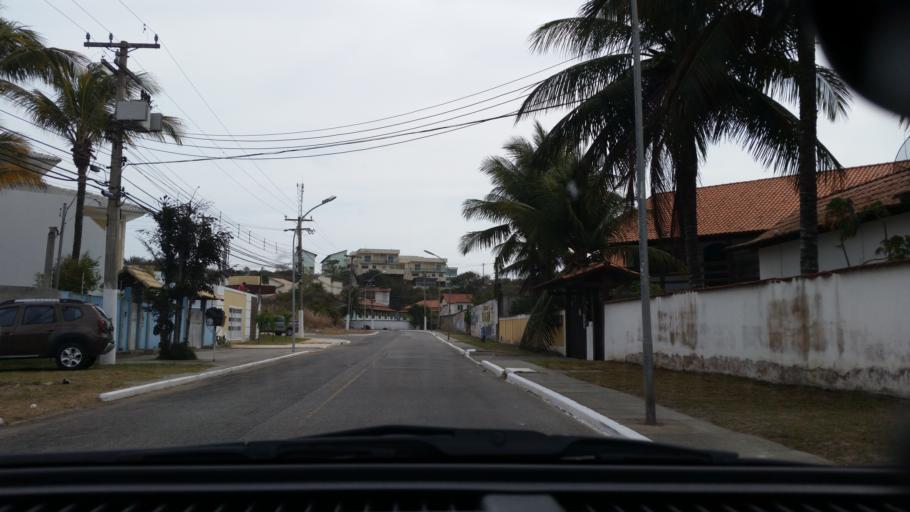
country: BR
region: Rio de Janeiro
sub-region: Cabo Frio
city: Cabo Frio
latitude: -22.8649
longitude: -41.9928
